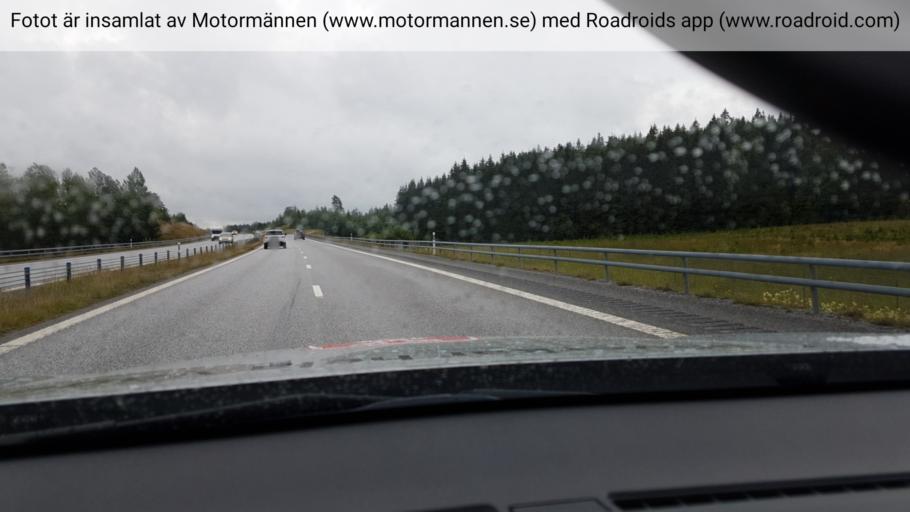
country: SE
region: Vaestra Goetaland
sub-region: Tanums Kommun
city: Tanumshede
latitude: 58.5766
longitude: 11.4534
